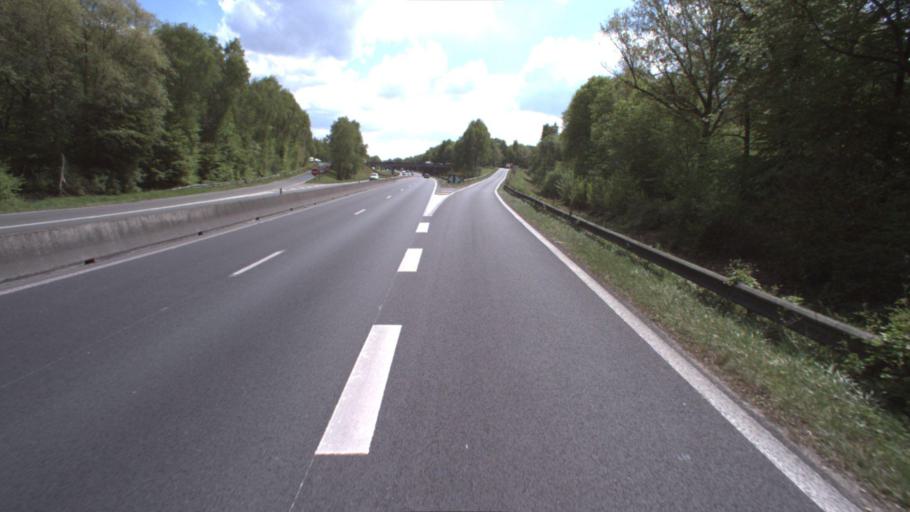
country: FR
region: Ile-de-France
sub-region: Departement de Seine-et-Marne
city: Gretz-Armainvilliers
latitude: 48.7384
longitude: 2.6982
